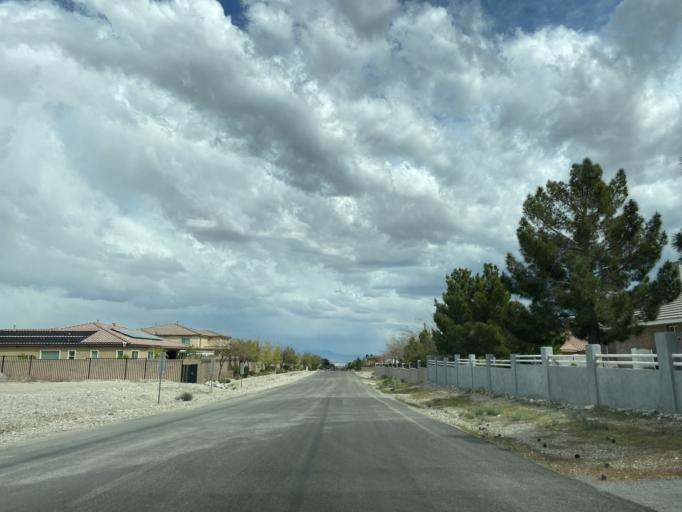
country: US
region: Nevada
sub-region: Clark County
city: Summerlin South
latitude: 36.2755
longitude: -115.3122
